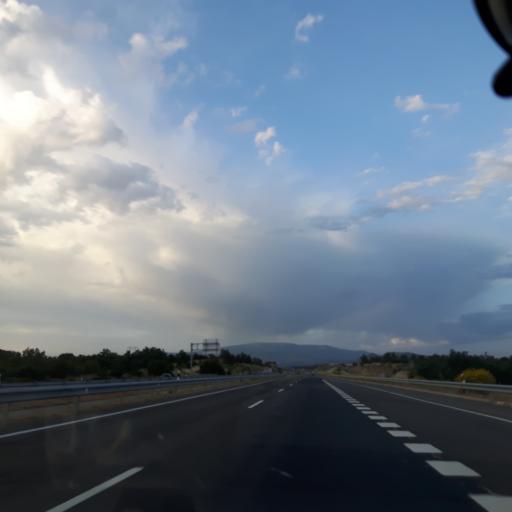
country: ES
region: Castille and Leon
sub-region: Provincia de Salamanca
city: Fuentes de Bejar
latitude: 40.5206
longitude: -5.6725
